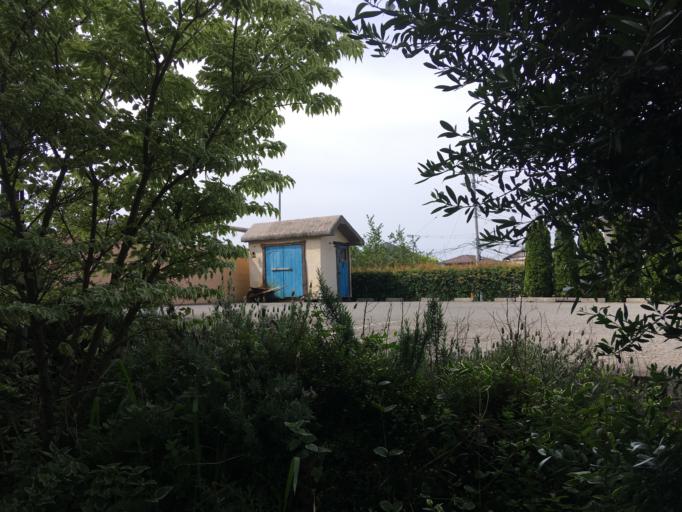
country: JP
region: Kanagawa
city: Minami-rinkan
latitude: 35.5085
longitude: 139.4699
